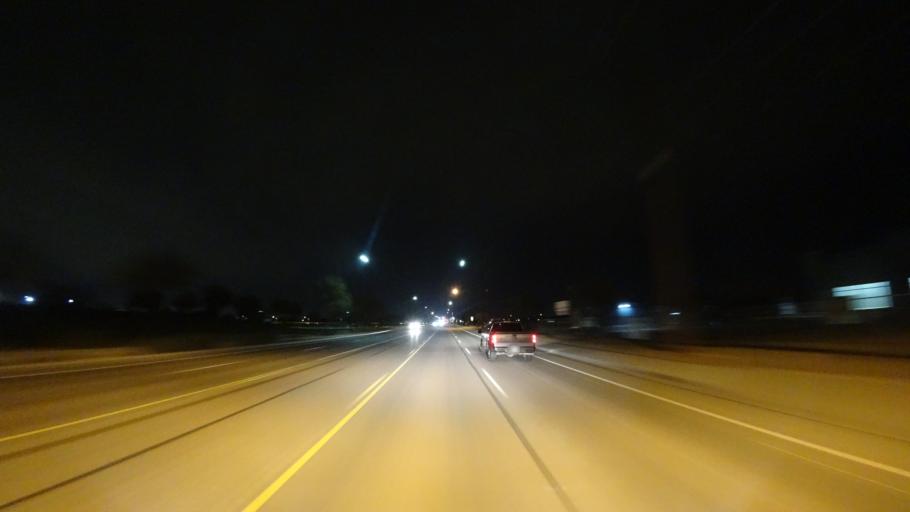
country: US
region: Arizona
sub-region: Maricopa County
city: Gilbert
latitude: 33.2712
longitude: -111.7379
